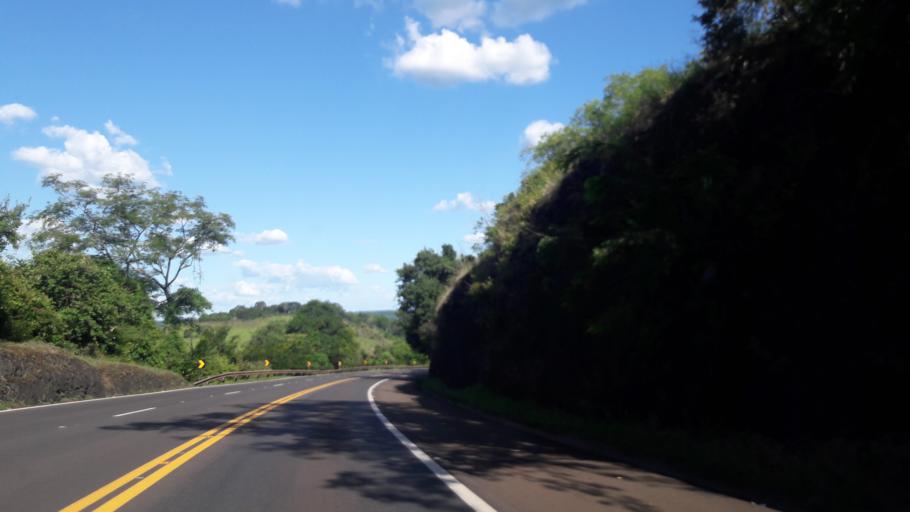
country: BR
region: Parana
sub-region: Laranjeiras Do Sul
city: Laranjeiras do Sul
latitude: -25.4052
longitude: -52.0942
